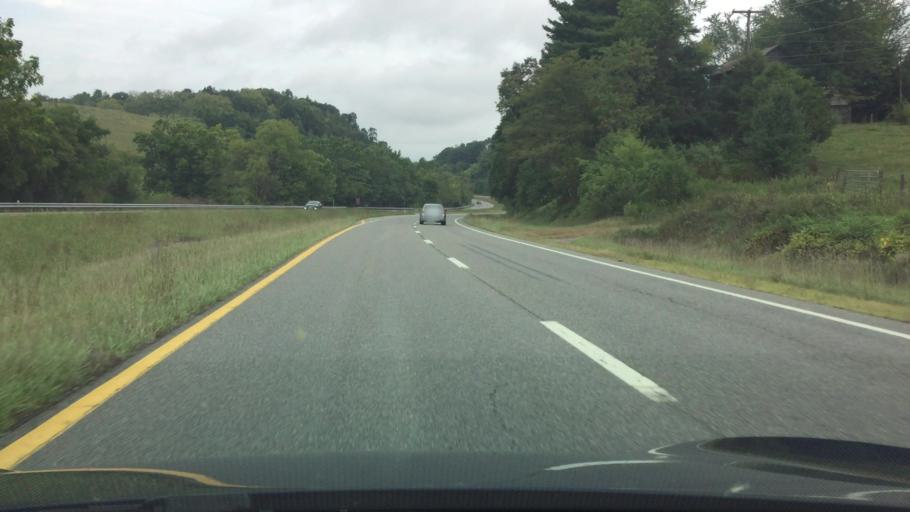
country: US
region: Virginia
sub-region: City of Radford
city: Radford
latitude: 37.1052
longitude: -80.5194
